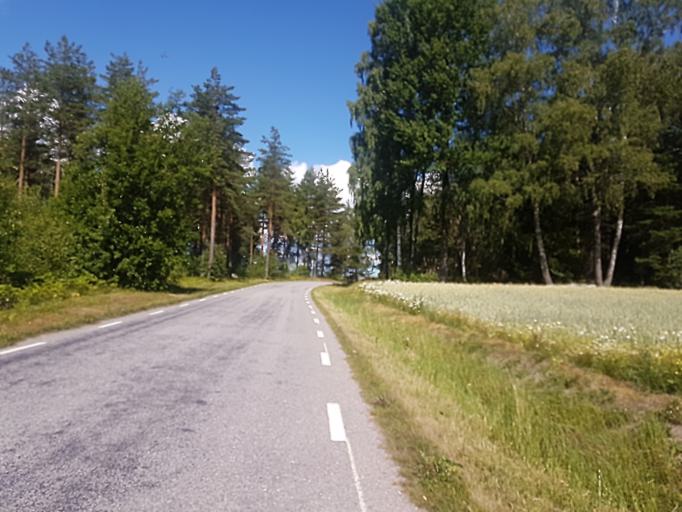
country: SE
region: Soedermanland
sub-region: Gnesta Kommun
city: Gnesta
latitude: 59.0366
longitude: 17.3488
